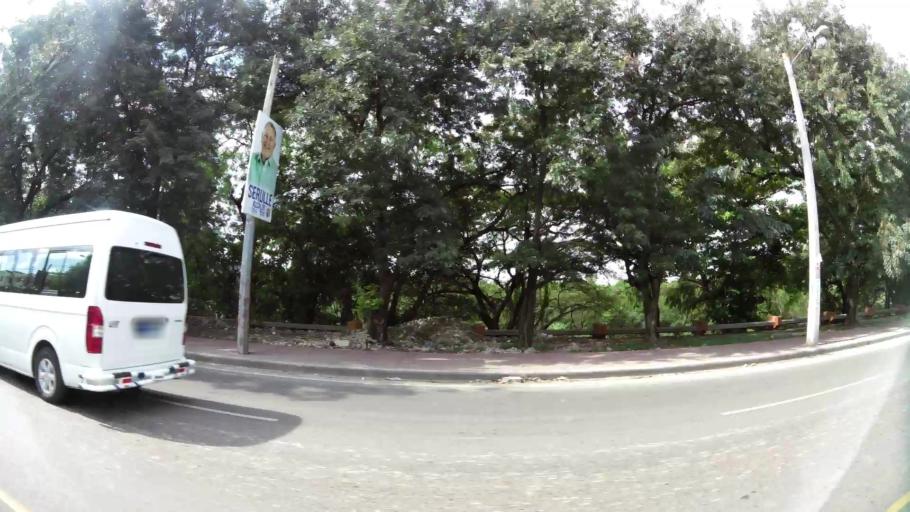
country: DO
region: Santiago
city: Santiago de los Caballeros
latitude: 19.4717
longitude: -70.7183
